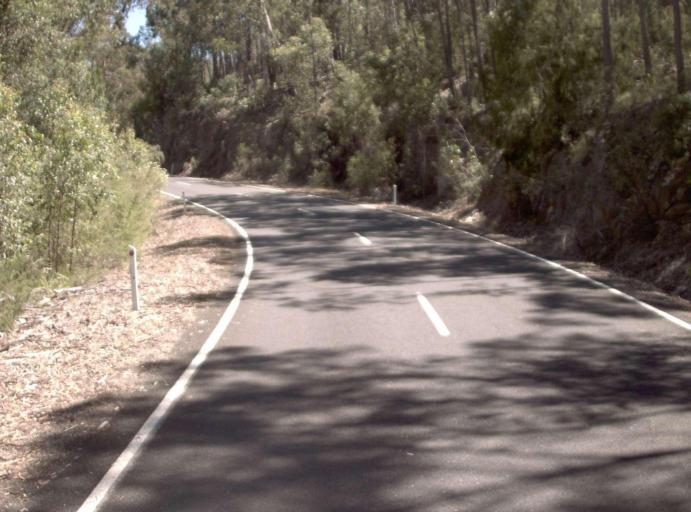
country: AU
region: Victoria
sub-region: East Gippsland
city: Lakes Entrance
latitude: -37.3790
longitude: 148.2171
